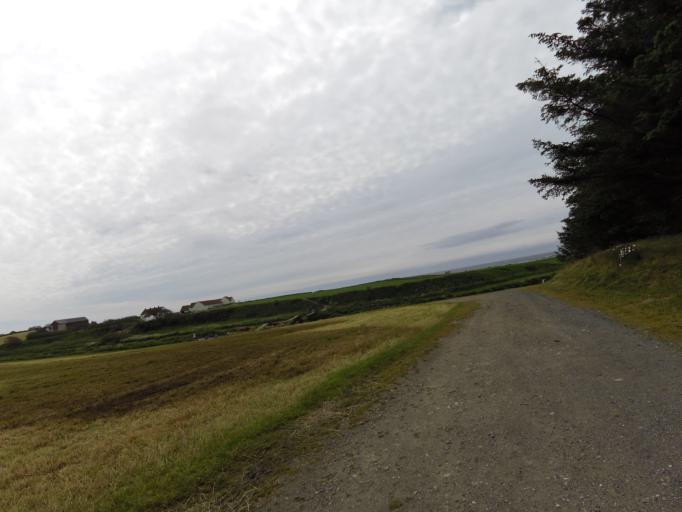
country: NO
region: Rogaland
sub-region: Ha
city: Naerbo
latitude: 58.6699
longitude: 5.5532
